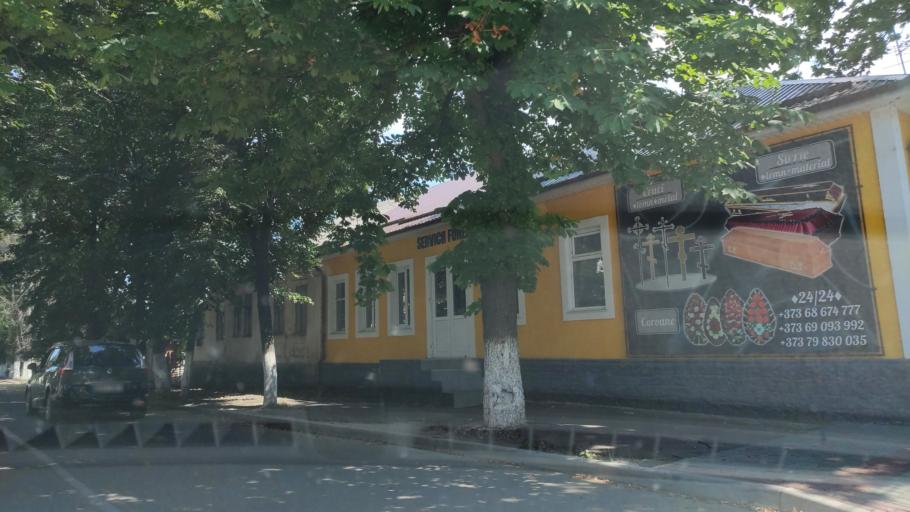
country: MD
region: Raionul Soroca
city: Soroca
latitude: 48.1515
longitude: 28.3003
